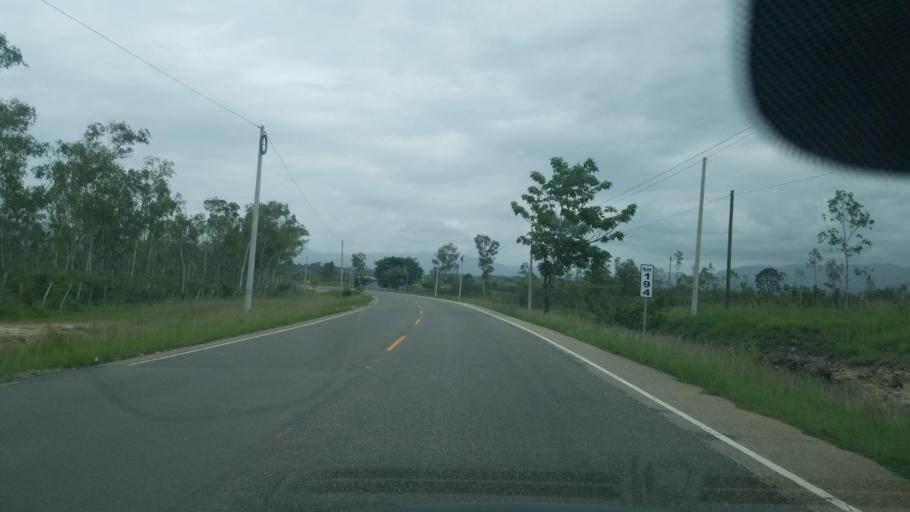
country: HN
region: Ocotepeque
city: Lucerna
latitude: 14.5287
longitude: -88.9514
